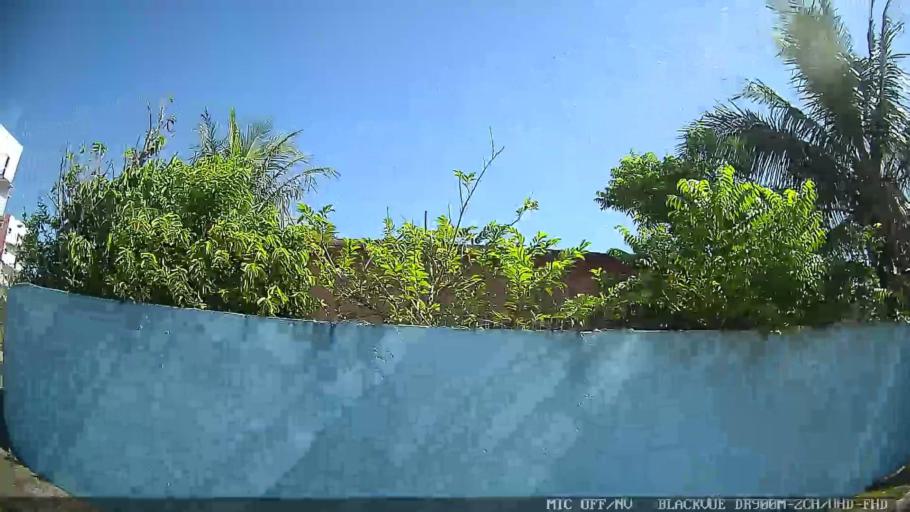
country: BR
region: Sao Paulo
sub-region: Peruibe
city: Peruibe
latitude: -24.2783
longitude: -46.9419
